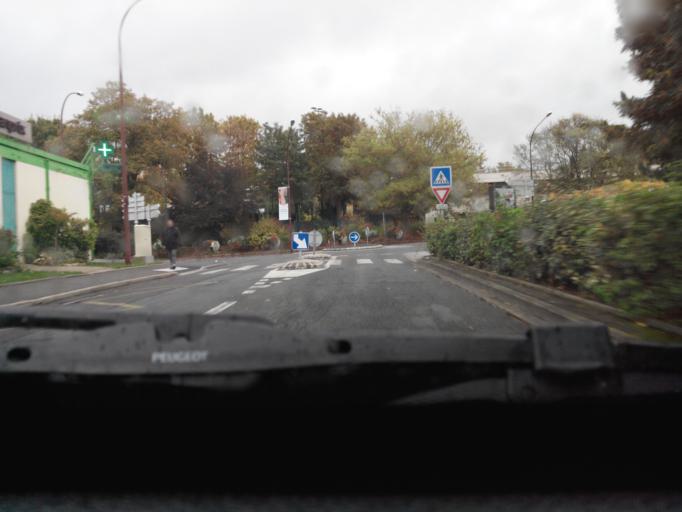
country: FR
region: Ile-de-France
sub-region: Departement du Val-de-Marne
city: L'Hay-les-Roses
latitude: 48.7860
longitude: 2.3322
